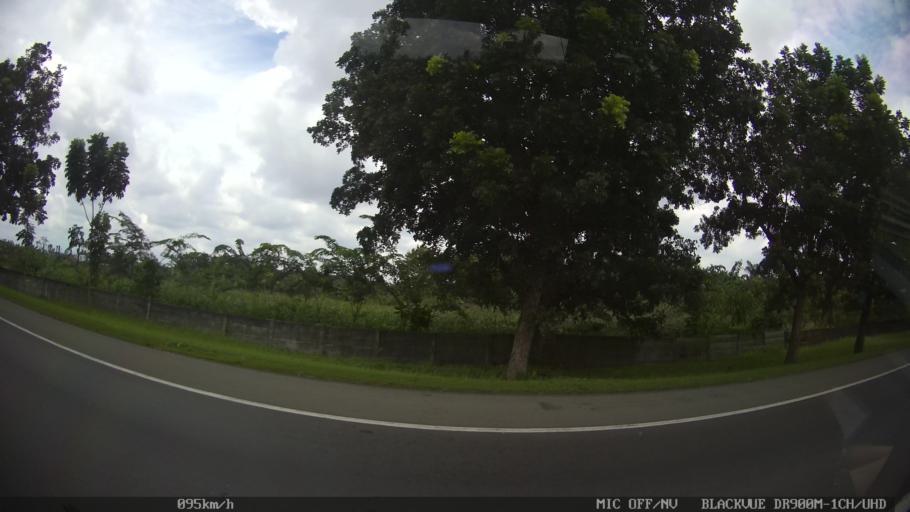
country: ID
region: North Sumatra
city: Medan
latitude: 3.6268
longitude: 98.7190
